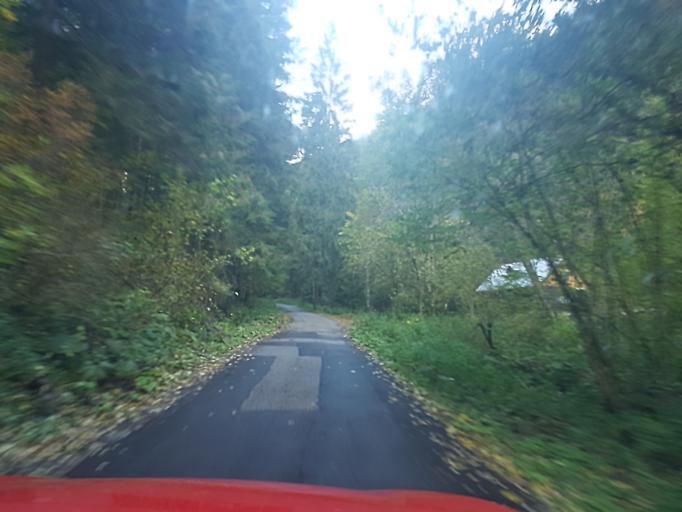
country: SK
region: Zilinsky
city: Ruzomberok
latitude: 48.9974
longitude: 19.2611
